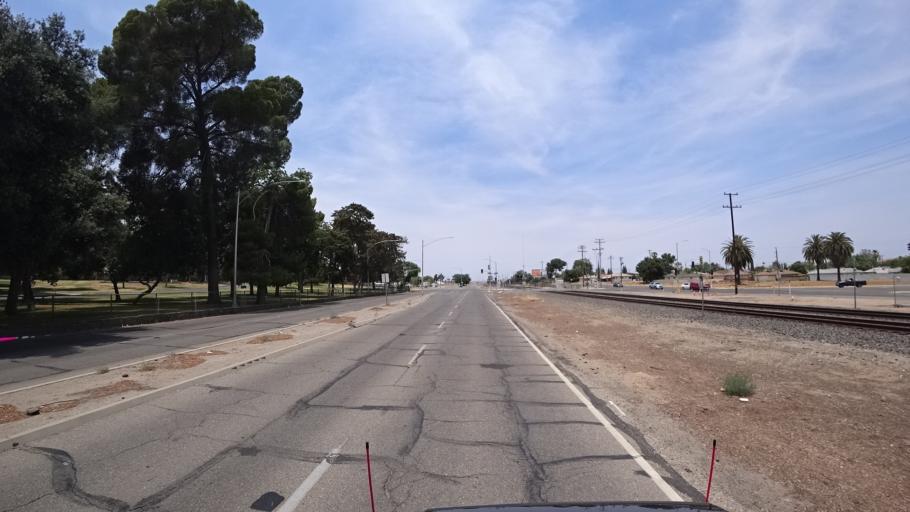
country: US
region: California
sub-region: Fresno County
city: Fresno
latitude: 36.7568
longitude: -119.8208
